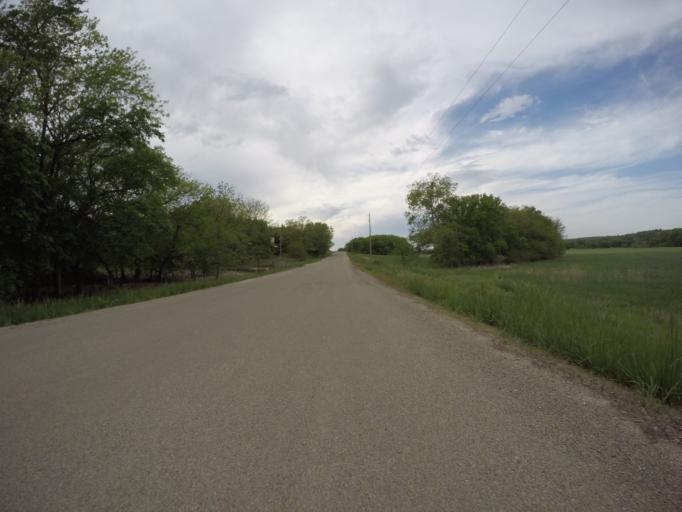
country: US
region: Kansas
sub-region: Riley County
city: Ogden
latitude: 39.0393
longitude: -96.6297
